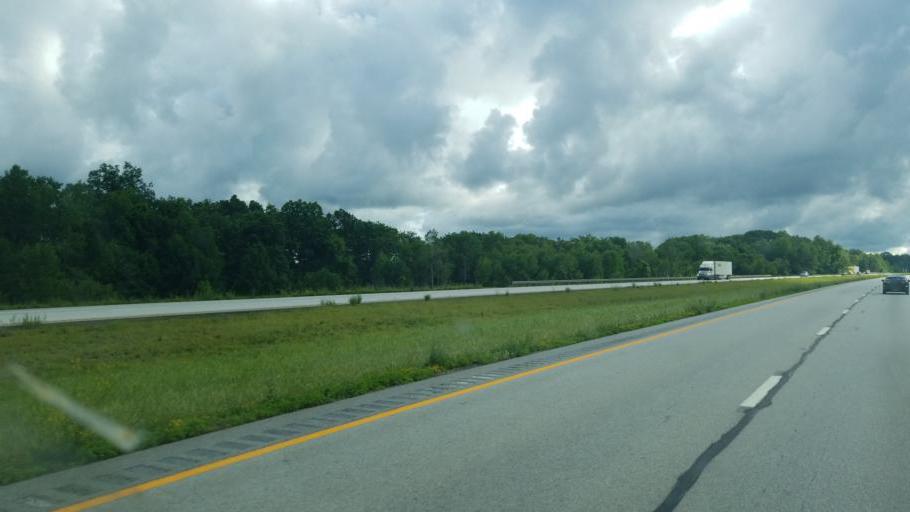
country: US
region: Ohio
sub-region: Ashtabula County
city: Edgewood
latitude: 41.8417
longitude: -80.7233
